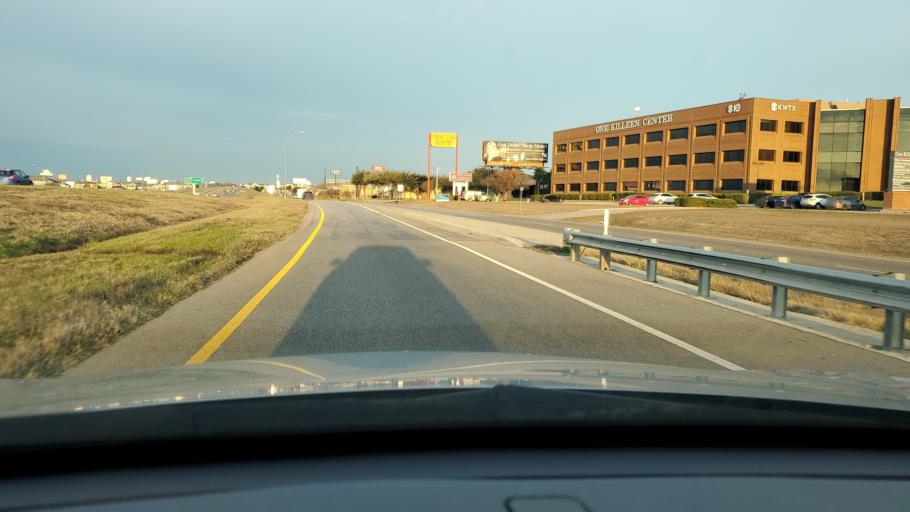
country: US
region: Texas
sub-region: Bell County
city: Killeen
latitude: 31.0923
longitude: -97.7221
